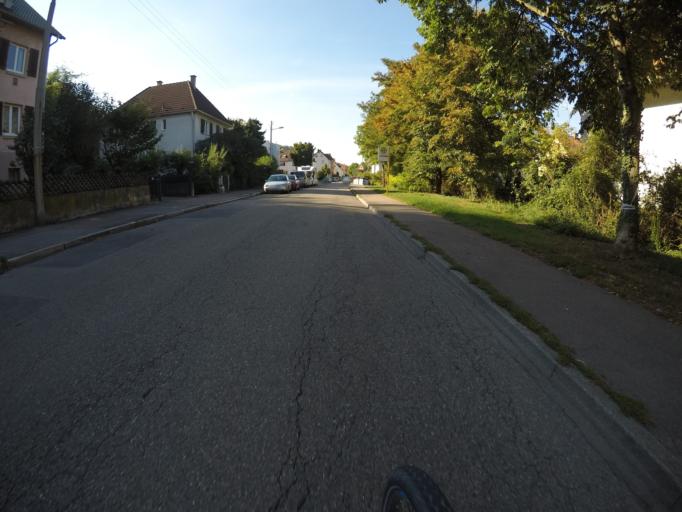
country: DE
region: Baden-Wuerttemberg
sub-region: Regierungsbezirk Stuttgart
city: Ostfildern
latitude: 48.7547
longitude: 9.2593
